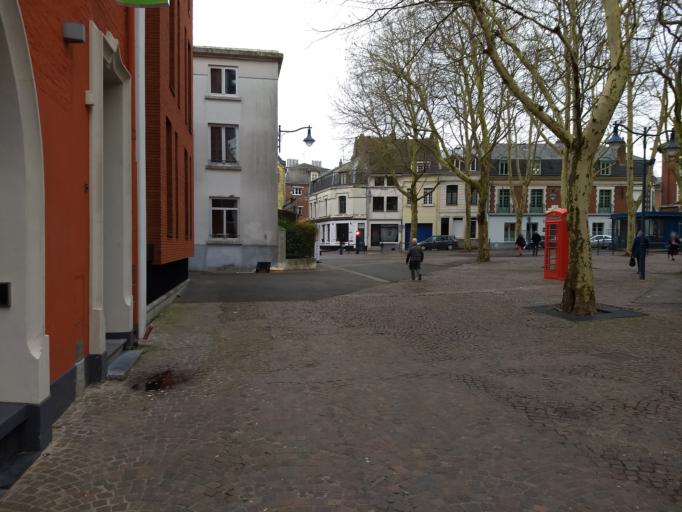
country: FR
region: Nord-Pas-de-Calais
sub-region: Departement du Pas-de-Calais
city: Arras
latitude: 50.2904
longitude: 2.7790
